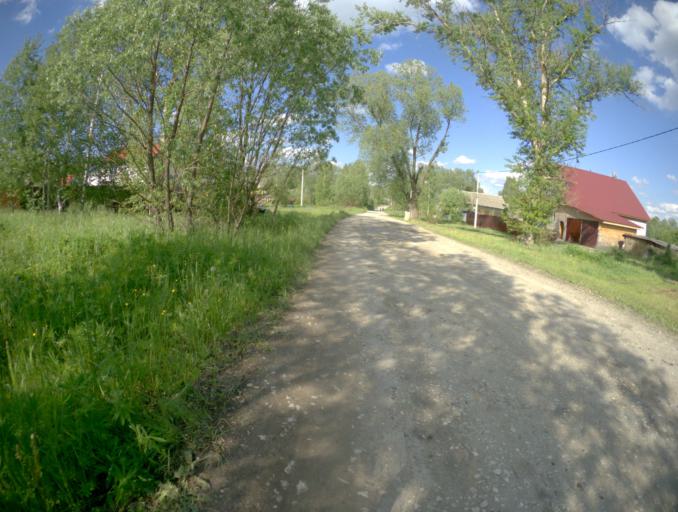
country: RU
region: Vladimir
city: Zolotkovo
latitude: 55.3306
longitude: 41.0058
